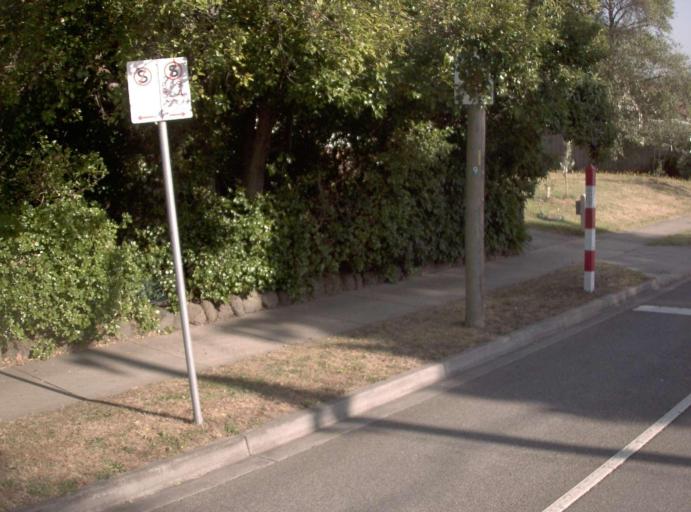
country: AU
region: Victoria
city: Carnegie
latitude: -37.8833
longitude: 145.0677
